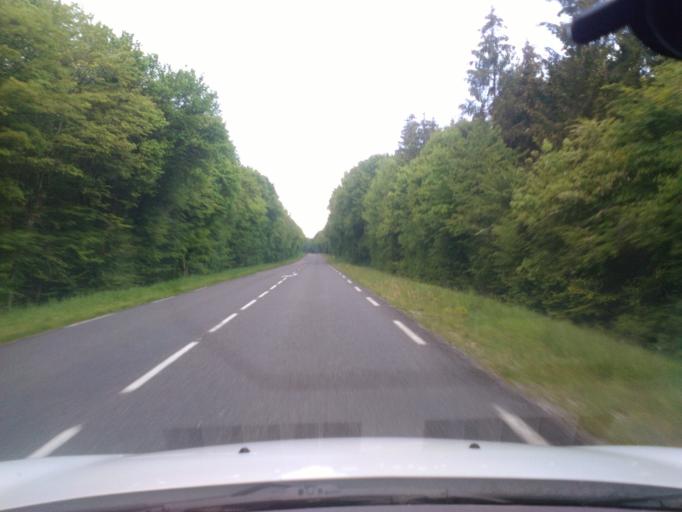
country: FR
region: Champagne-Ardenne
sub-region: Departement de la Haute-Marne
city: Lavilleneuve-au-Roi
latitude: 48.2119
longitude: 4.9210
